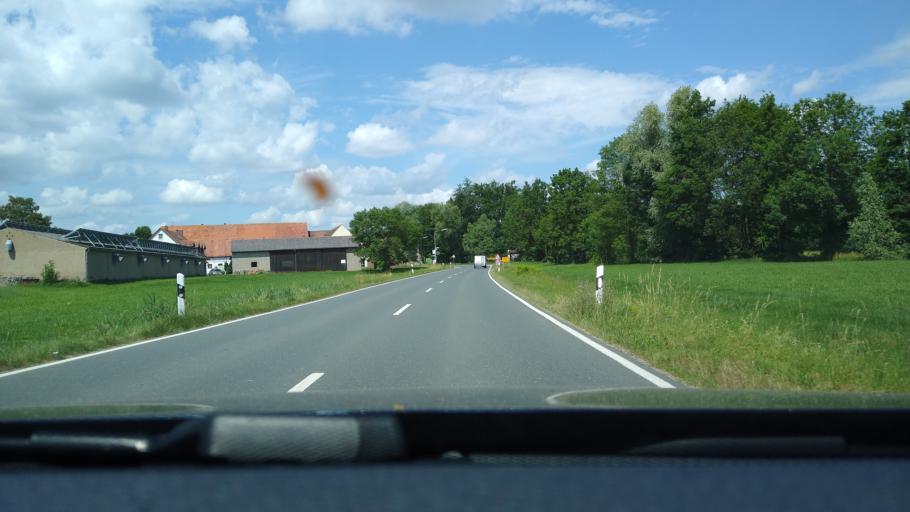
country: DE
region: Bavaria
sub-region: Regierungsbezirk Mittelfranken
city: Trautskirchen
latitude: 49.4623
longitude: 10.5672
